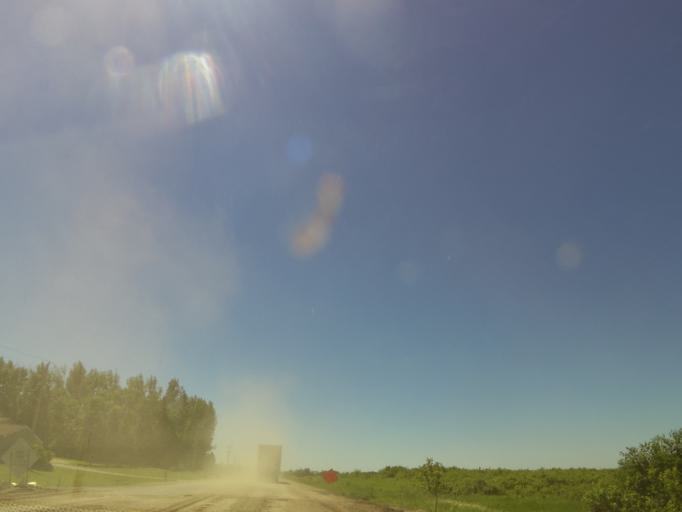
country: US
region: Minnesota
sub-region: Mahnomen County
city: Mahnomen
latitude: 47.1252
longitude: -95.9270
